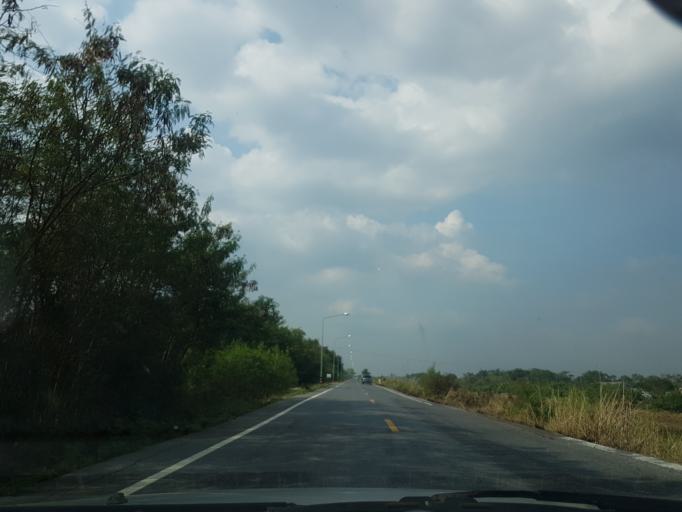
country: TH
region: Phra Nakhon Si Ayutthaya
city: Phachi
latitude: 14.4560
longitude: 100.7577
